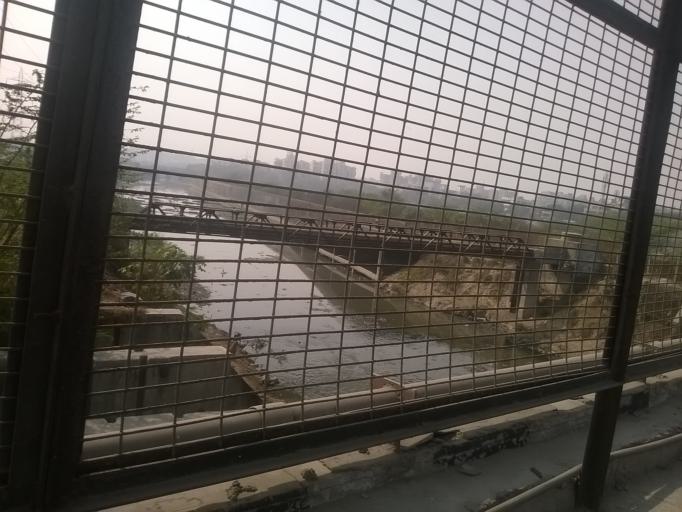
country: IN
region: NCT
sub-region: West Delhi
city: Nangloi Jat
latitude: 28.5993
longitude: 77.0620
